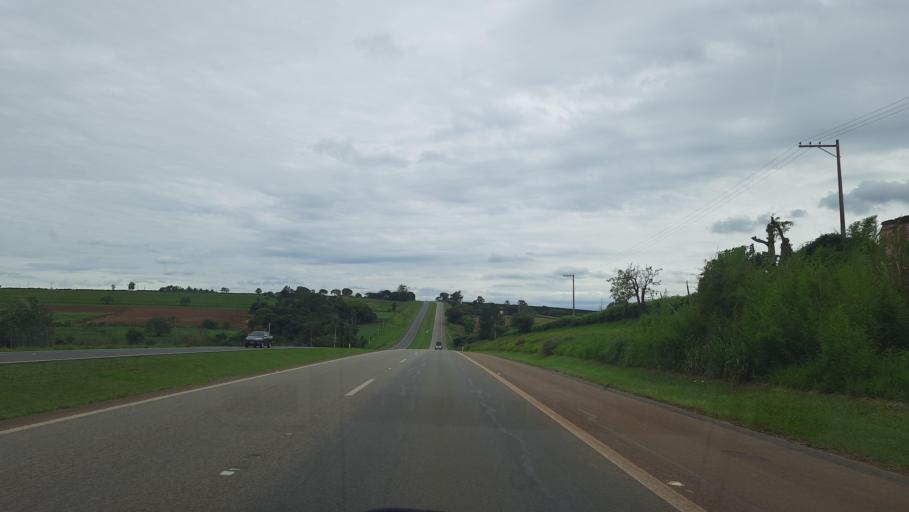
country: BR
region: Sao Paulo
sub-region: Moji-Guacu
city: Mogi-Gaucu
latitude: -22.2435
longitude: -46.9781
